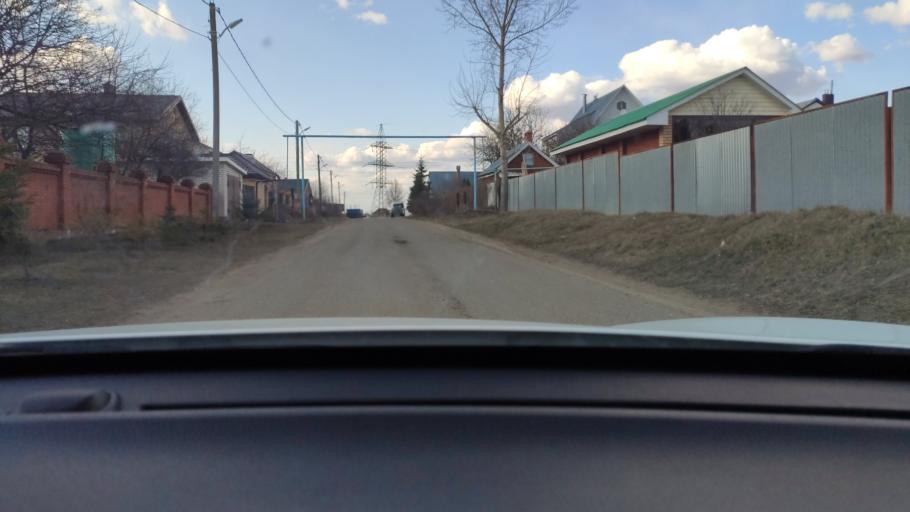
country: RU
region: Tatarstan
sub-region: Gorod Kazan'
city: Kazan
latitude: 55.8103
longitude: 49.2187
